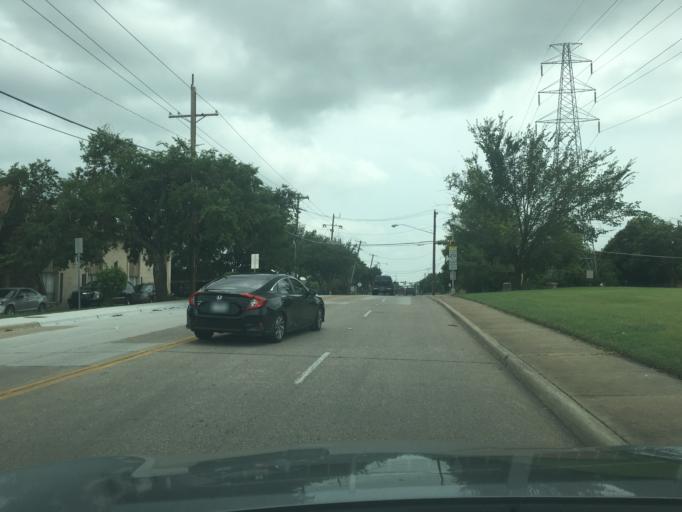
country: US
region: Texas
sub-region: Dallas County
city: Richardson
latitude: 32.9391
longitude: -96.7612
